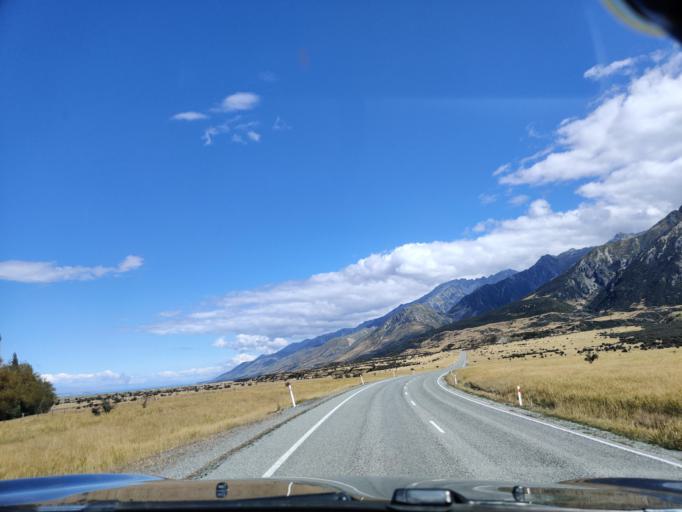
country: NZ
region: Canterbury
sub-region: Timaru District
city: Pleasant Point
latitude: -43.7901
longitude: 170.1195
